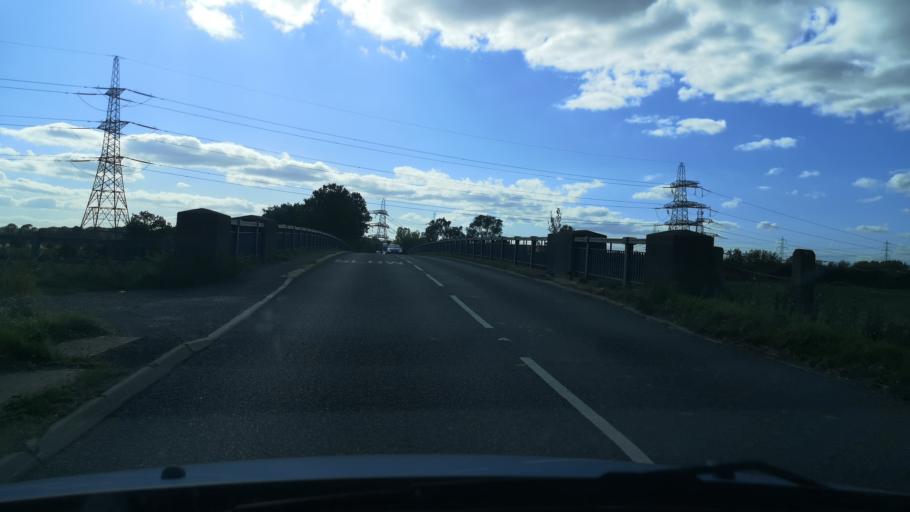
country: GB
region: England
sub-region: Doncaster
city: Kirk Sandall
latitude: 53.5766
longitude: -1.0808
